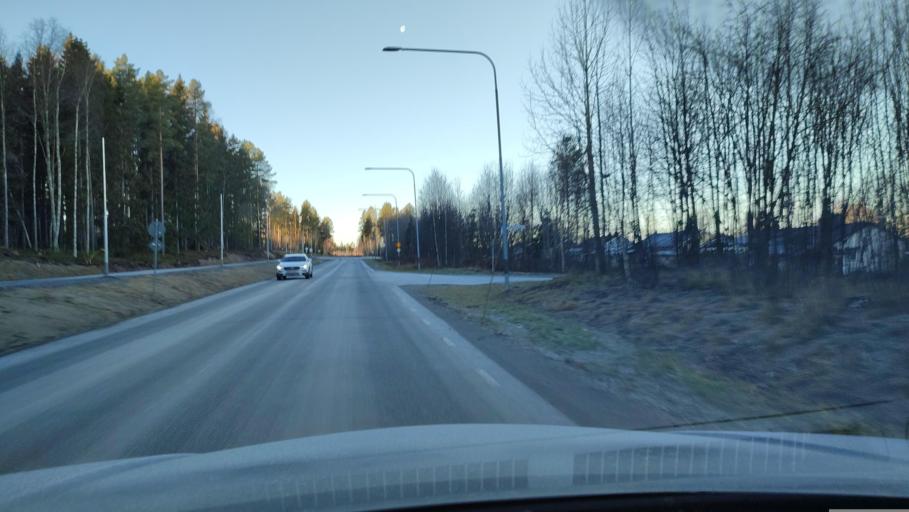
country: SE
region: Vaesterbotten
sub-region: Skelleftea Kommun
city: Viken
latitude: 64.7403
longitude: 20.9233
